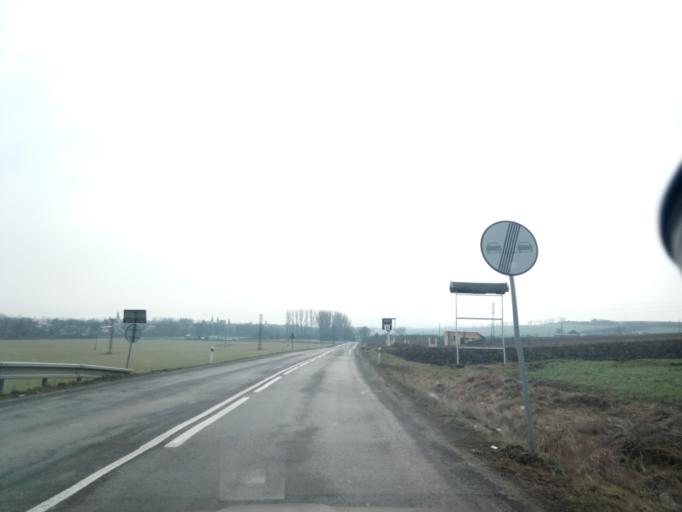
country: SK
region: Kosicky
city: Secovce
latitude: 48.6115
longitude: 21.6155
